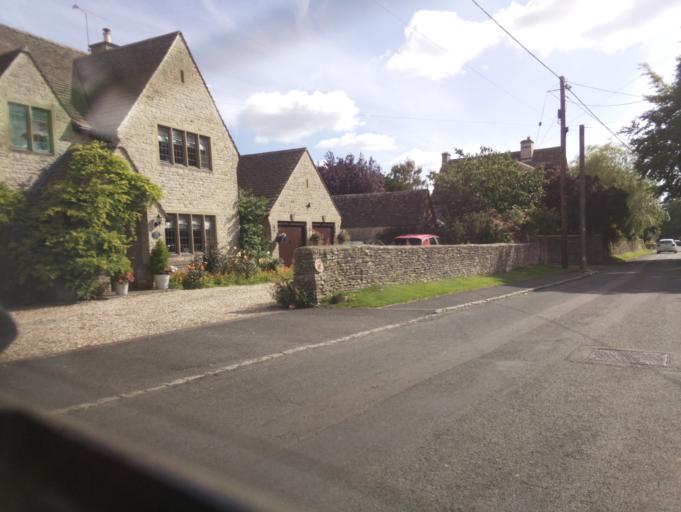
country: GB
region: England
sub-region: Gloucestershire
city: Coates
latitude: 51.7076
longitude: -2.0311
